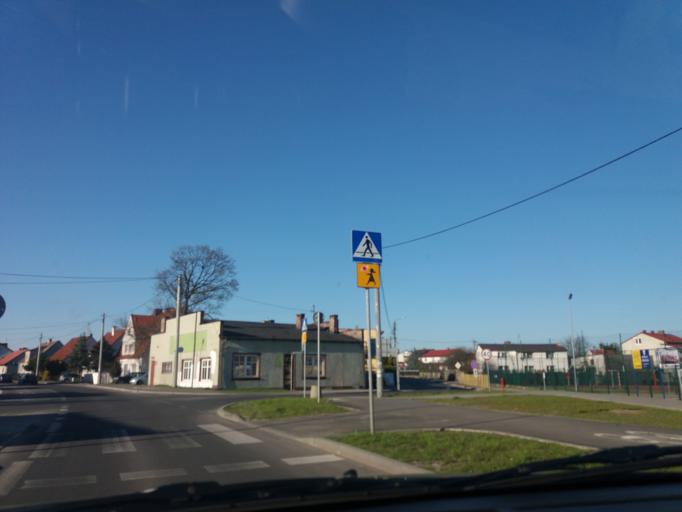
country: PL
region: Warmian-Masurian Voivodeship
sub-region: Powiat nidzicki
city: Nidzica
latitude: 53.3674
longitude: 20.4297
